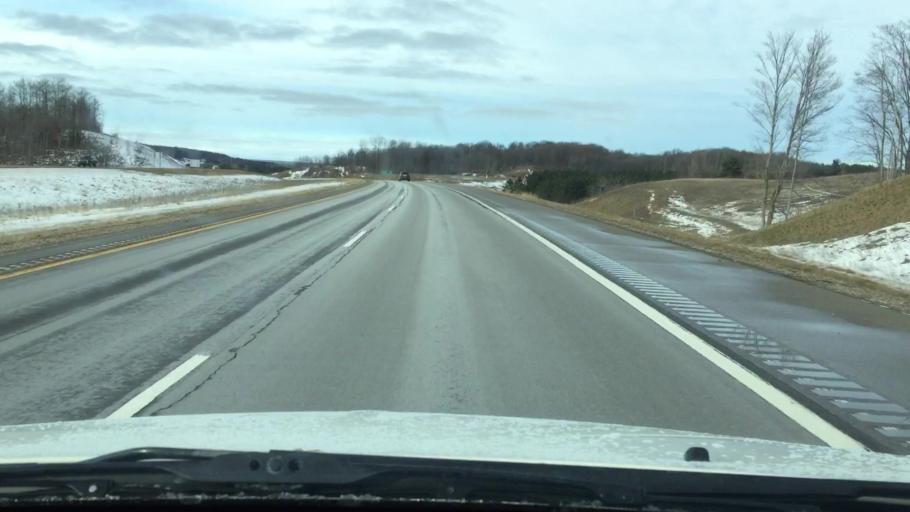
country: US
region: Michigan
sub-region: Wexford County
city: Manton
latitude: 44.4160
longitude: -85.3805
